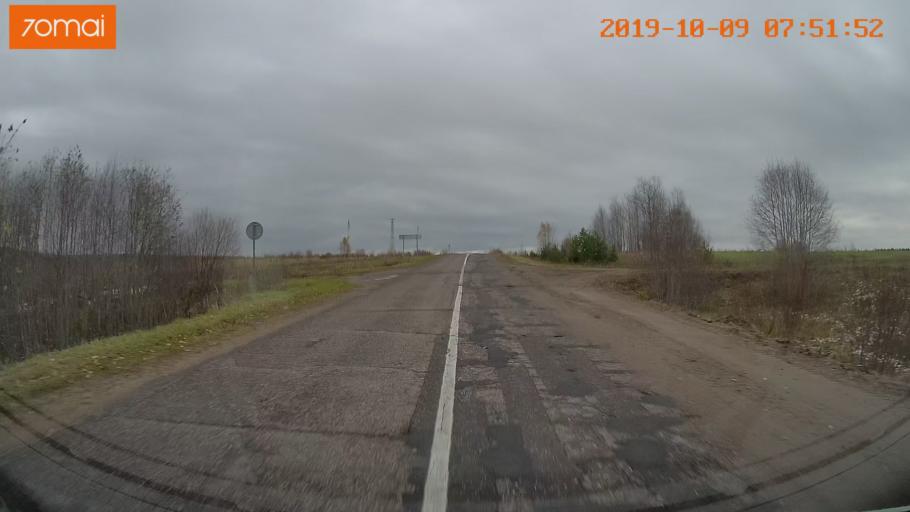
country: RU
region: Jaroslavl
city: Kukoboy
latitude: 58.6864
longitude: 39.8820
